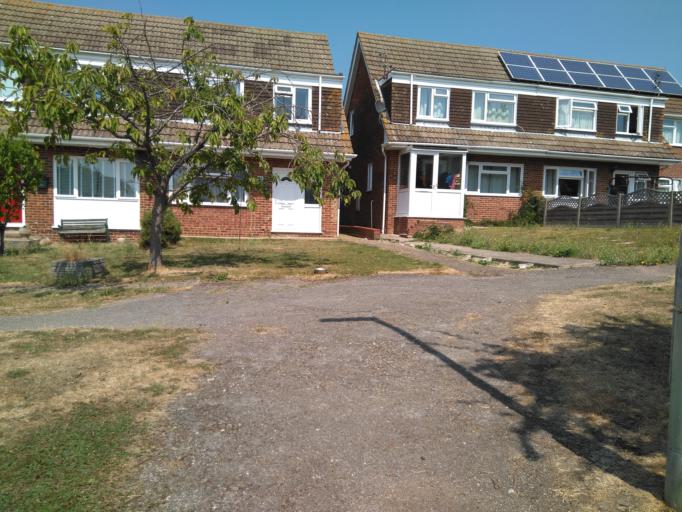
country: GB
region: England
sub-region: Kent
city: Whitstable
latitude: 51.3433
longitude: 1.0097
